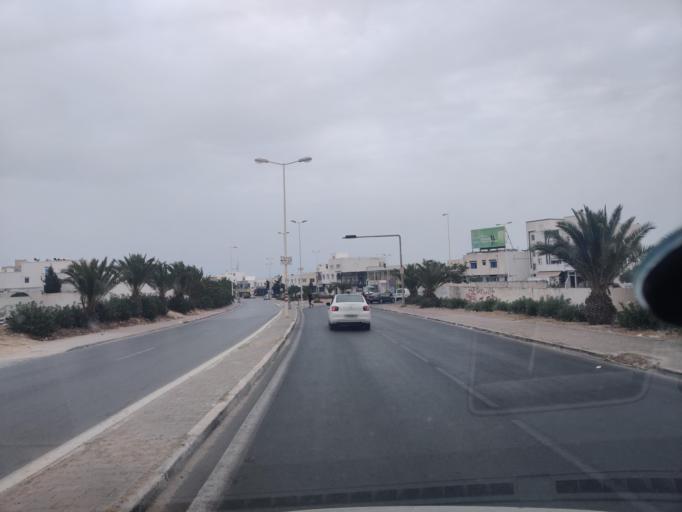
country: TN
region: Nabul
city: Al Hammamat
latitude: 36.4078
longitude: 10.6359
